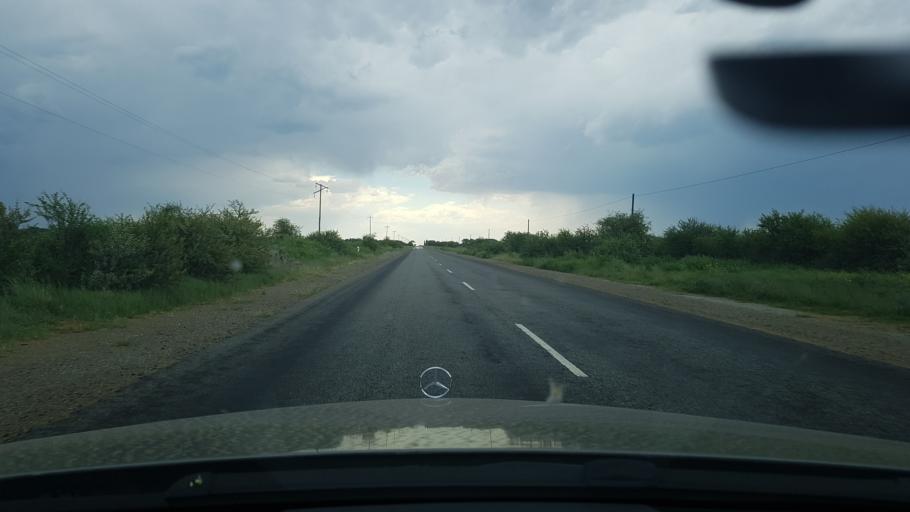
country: ZA
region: Orange Free State
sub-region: Lejweleputswa District Municipality
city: Hoopstad
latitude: -27.9810
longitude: 25.6641
